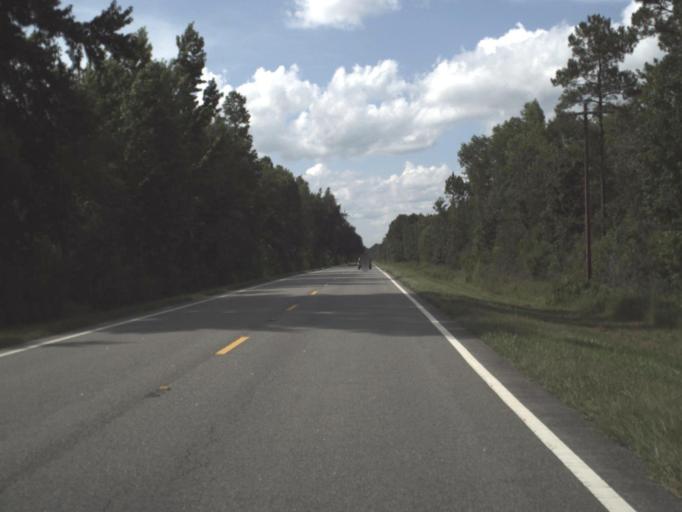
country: US
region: Florida
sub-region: Taylor County
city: Perry
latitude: 30.3247
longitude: -83.6422
